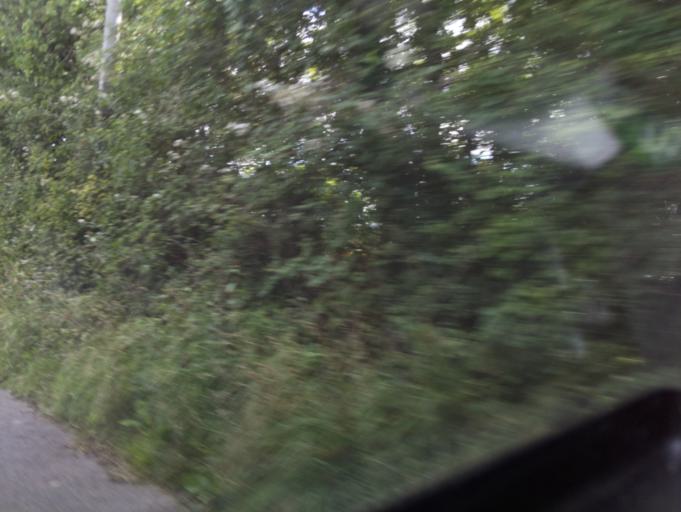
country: GB
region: England
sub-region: Gloucestershire
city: Cinderford
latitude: 51.8319
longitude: -2.4479
